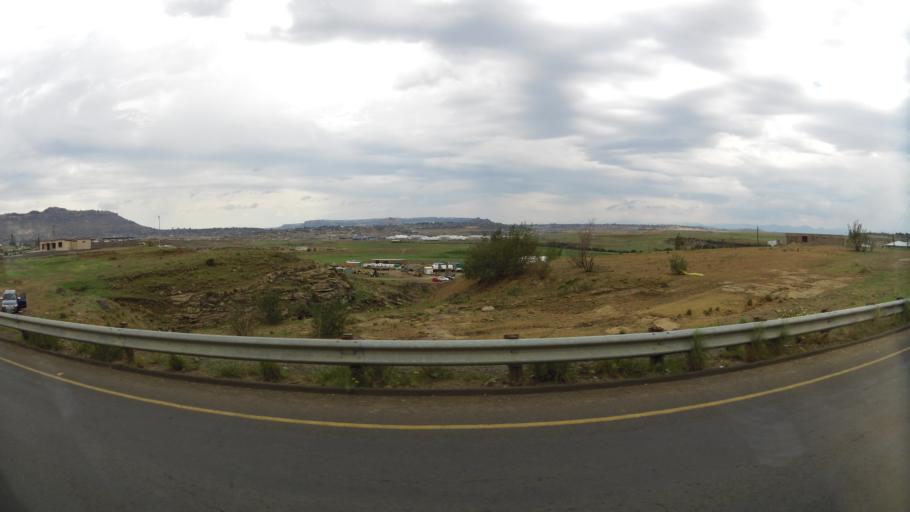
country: LS
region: Maseru
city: Maseru
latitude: -29.3892
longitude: 27.4706
